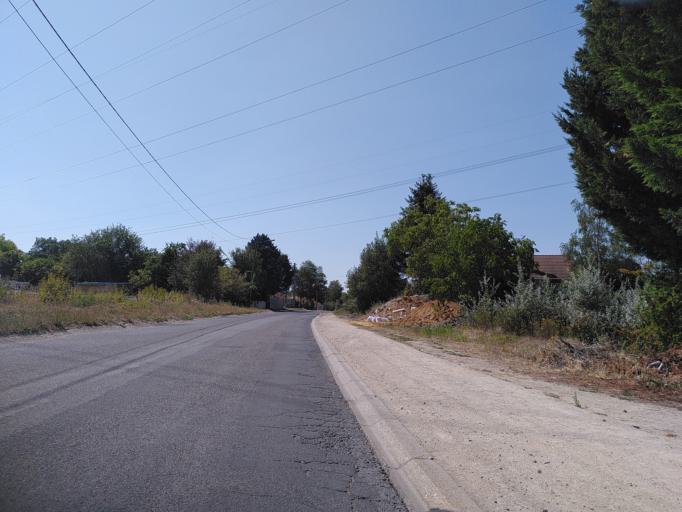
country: FR
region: Ile-de-France
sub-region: Departement de l'Essonne
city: Saint-Germain-les-Arpajon
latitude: 48.6039
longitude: 2.2678
